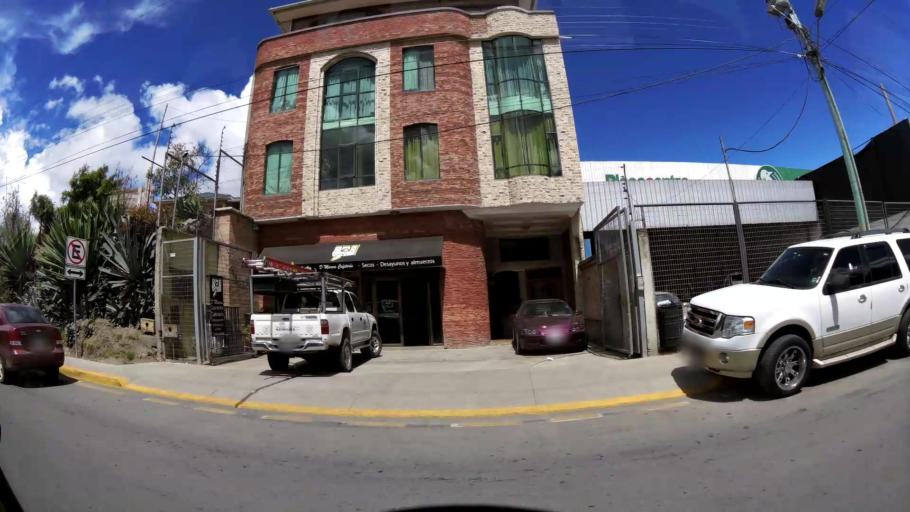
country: EC
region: Canar
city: Azogues
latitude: -2.7489
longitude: -78.8509
